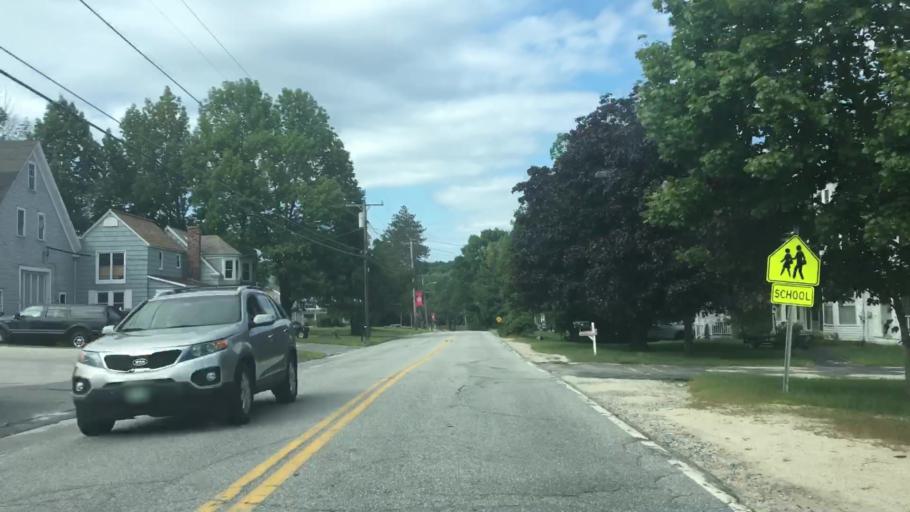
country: US
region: Maine
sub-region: Cumberland County
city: Raymond
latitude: 44.0071
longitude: -70.5227
